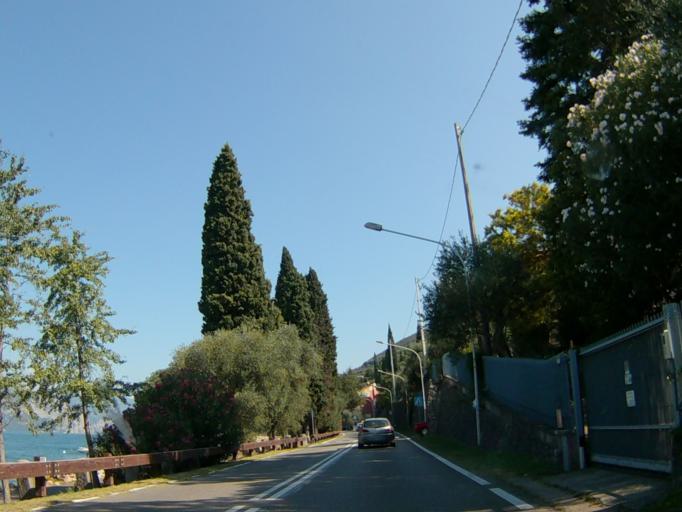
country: IT
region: Veneto
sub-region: Provincia di Verona
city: San Zeno di Montagna
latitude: 45.6499
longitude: 10.7199
